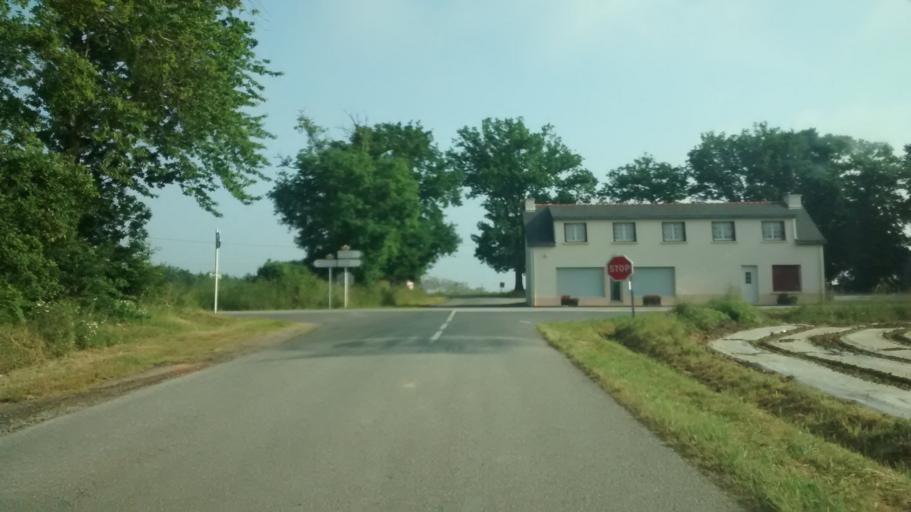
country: FR
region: Brittany
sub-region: Departement du Morbihan
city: Ruffiac
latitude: 47.8463
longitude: -2.2757
